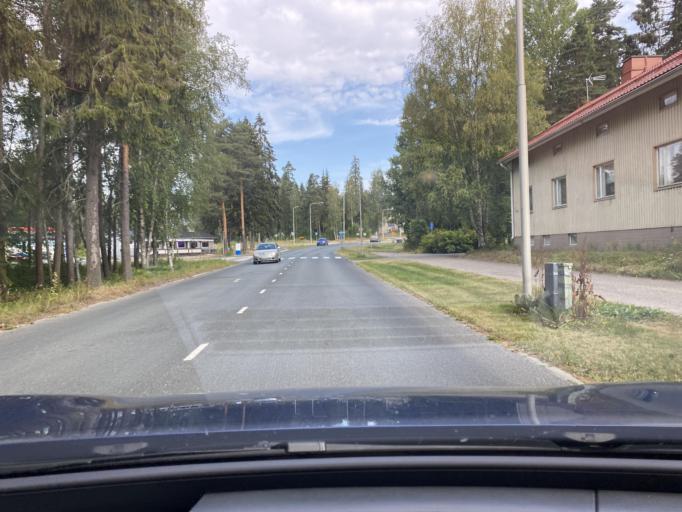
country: FI
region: Pirkanmaa
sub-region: Lounais-Pirkanmaa
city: Vammala
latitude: 61.3541
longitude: 22.8930
